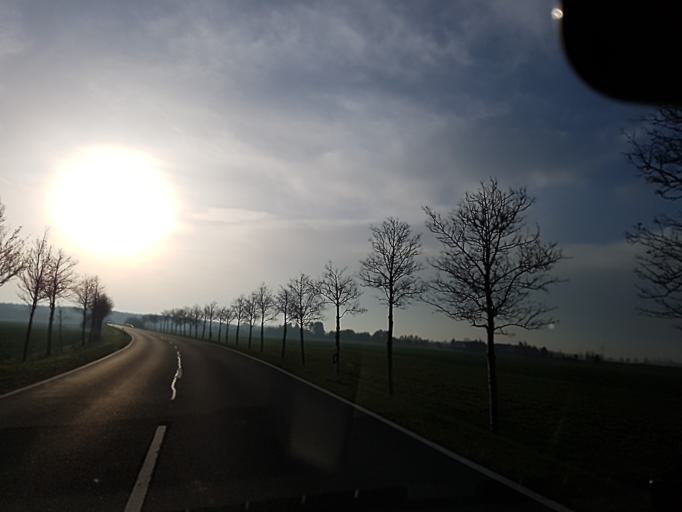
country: DE
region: Saxony
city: Riesa
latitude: 51.3508
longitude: 13.2762
